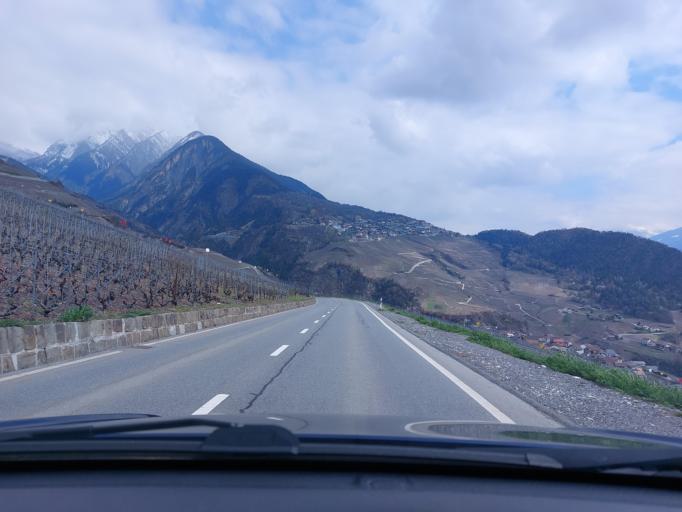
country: CH
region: Valais
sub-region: Conthey District
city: Conthey
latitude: 46.2392
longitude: 7.2981
